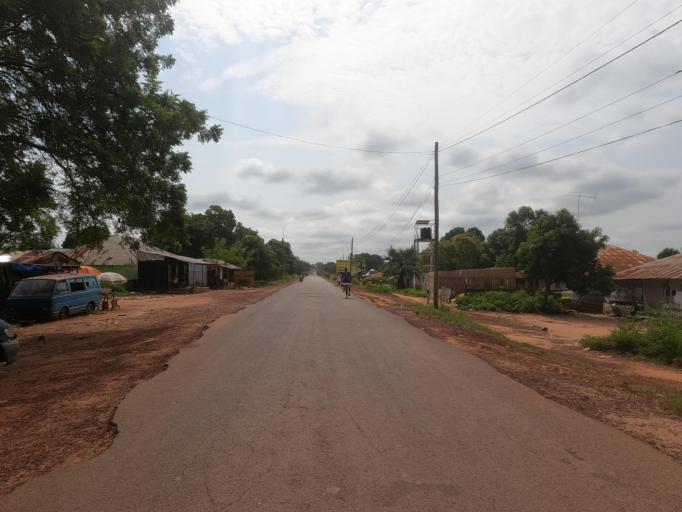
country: SN
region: Ziguinchor
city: Adeane
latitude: 12.4018
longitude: -15.7922
